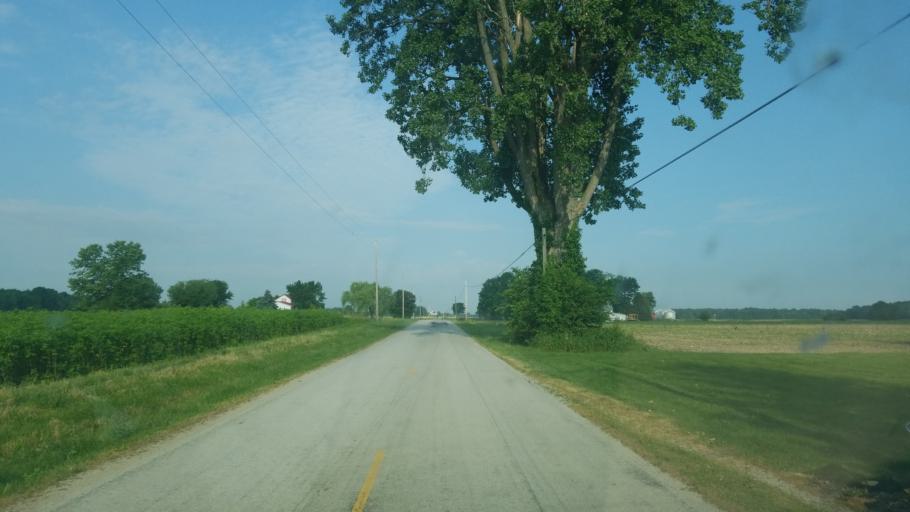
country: US
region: Ohio
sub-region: Hardin County
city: Kenton
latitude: 40.6283
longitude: -83.6944
